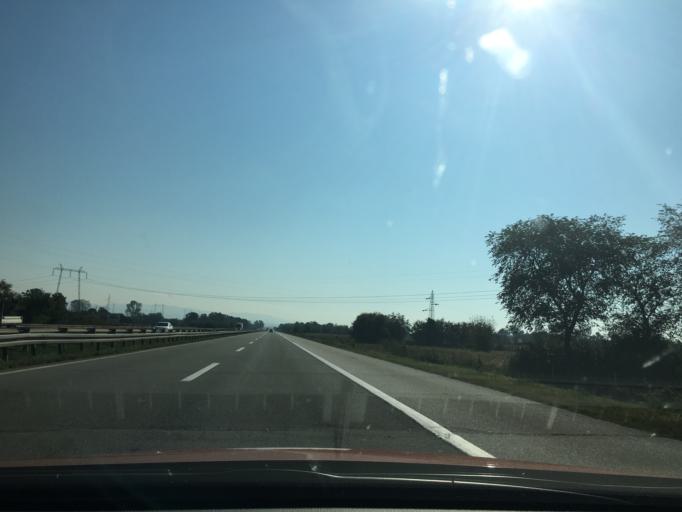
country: RS
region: Central Serbia
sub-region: Pomoravski Okrug
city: Cuprija
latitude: 43.9629
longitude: 21.3290
